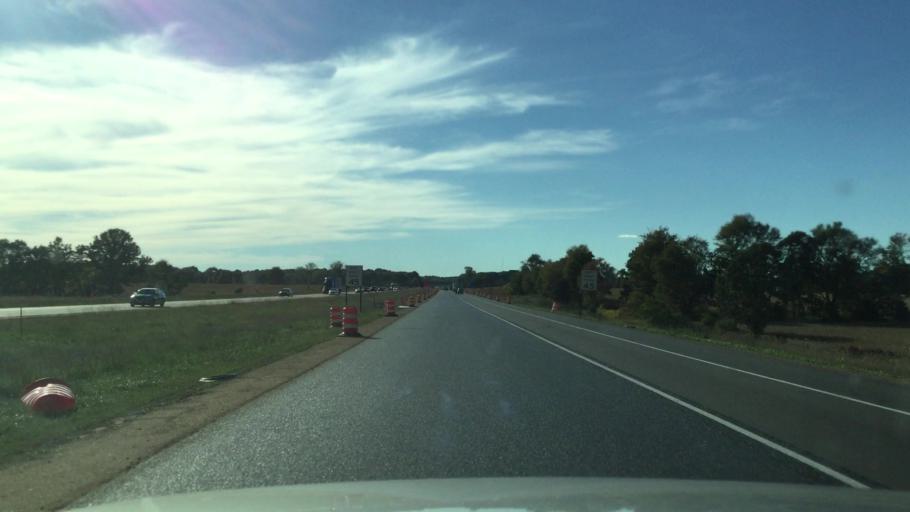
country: US
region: Michigan
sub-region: Calhoun County
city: Marshall
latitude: 42.2829
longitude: -84.8948
